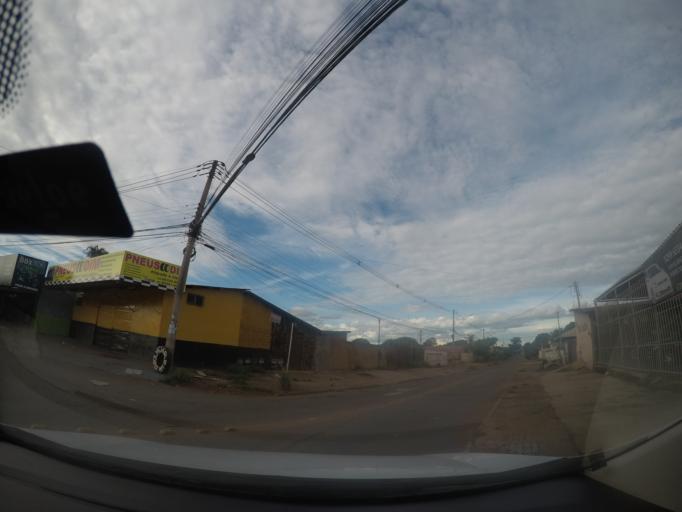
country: BR
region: Goias
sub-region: Goiania
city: Goiania
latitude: -16.6495
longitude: -49.3346
